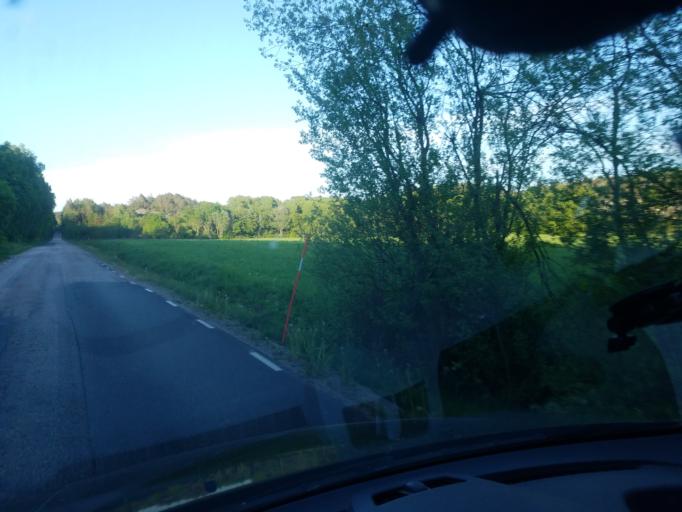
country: SE
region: Vaestra Goetaland
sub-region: Orust
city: Henan
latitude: 58.2872
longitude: 11.6178
